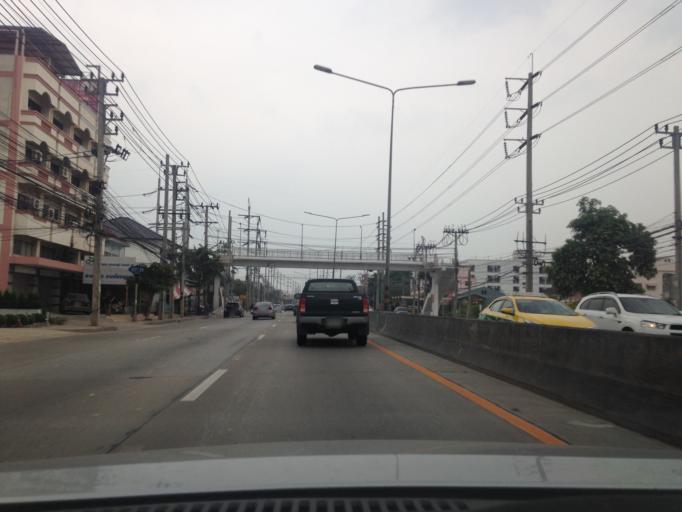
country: TH
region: Bangkok
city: Lat Krabang
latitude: 13.7415
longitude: 100.7466
